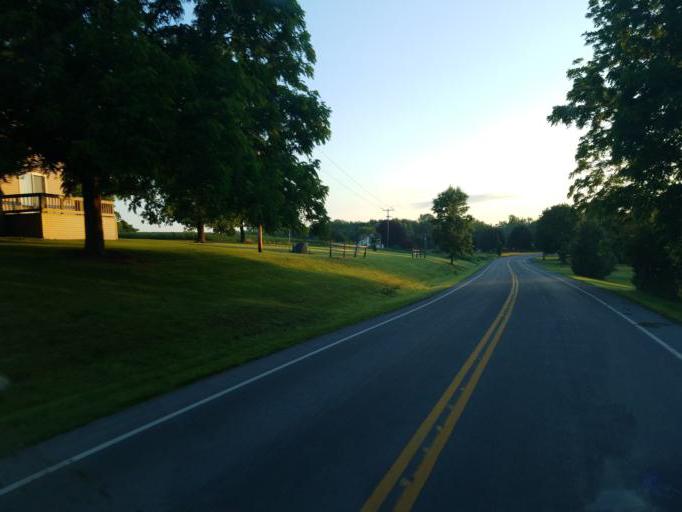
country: US
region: New York
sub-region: Wayne County
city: Clyde
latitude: 43.0794
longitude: -76.8914
